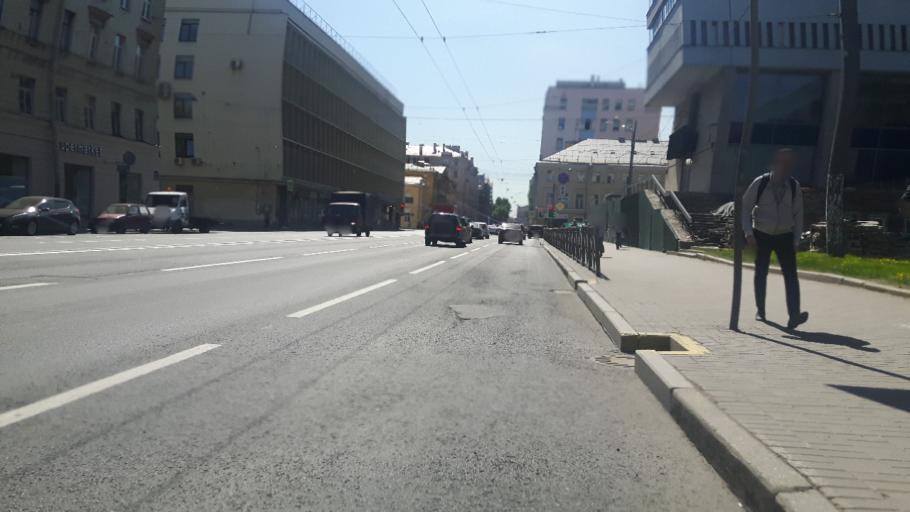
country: RU
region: St.-Petersburg
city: Admiralteisky
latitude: 59.9149
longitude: 30.2973
